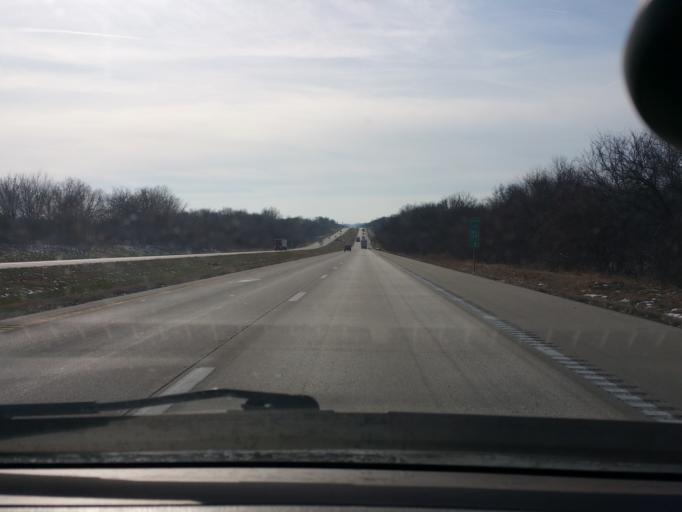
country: US
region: Missouri
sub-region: Clay County
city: Kearney
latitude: 39.4172
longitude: -94.3457
